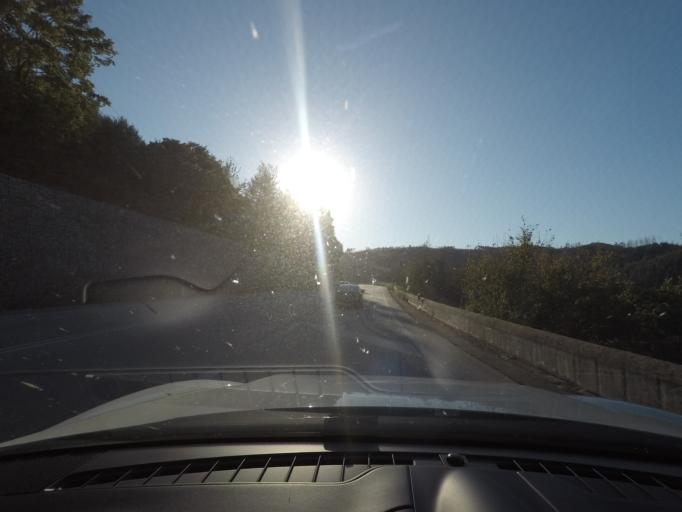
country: PT
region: Coimbra
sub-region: Vila Nova de Poiares
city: Poiares
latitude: 40.1750
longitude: -8.3205
